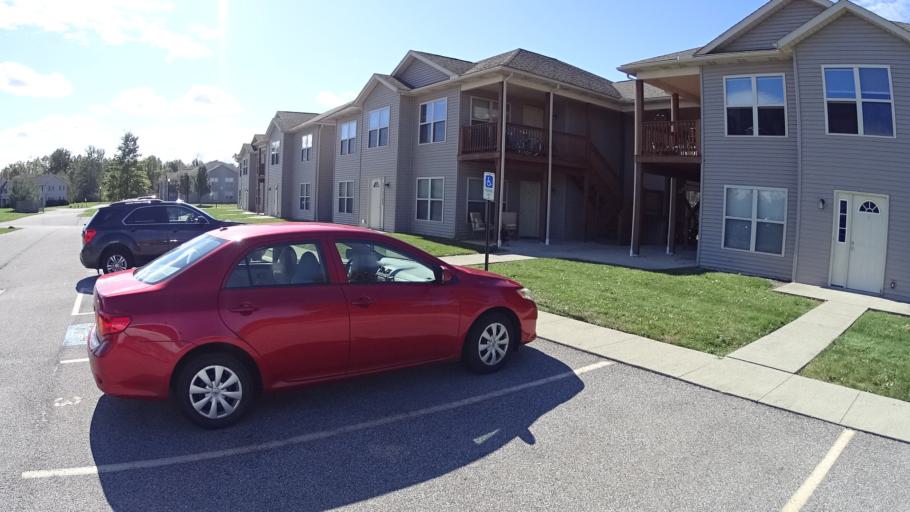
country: US
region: Ohio
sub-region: Lorain County
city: Grafton
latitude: 41.2800
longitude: -82.0646
